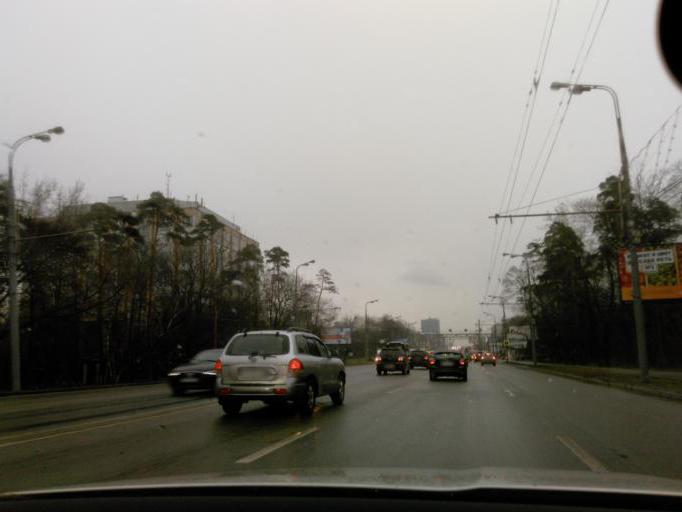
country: RU
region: Moscow
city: Pokrovskoye-Streshnevo
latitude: 55.8119
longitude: 37.4801
